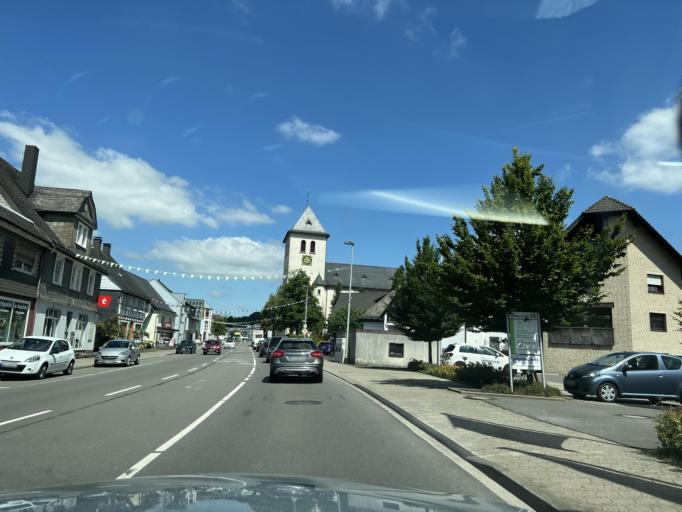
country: DE
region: North Rhine-Westphalia
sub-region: Regierungsbezirk Arnsberg
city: Wenden
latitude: 50.9852
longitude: 7.8470
